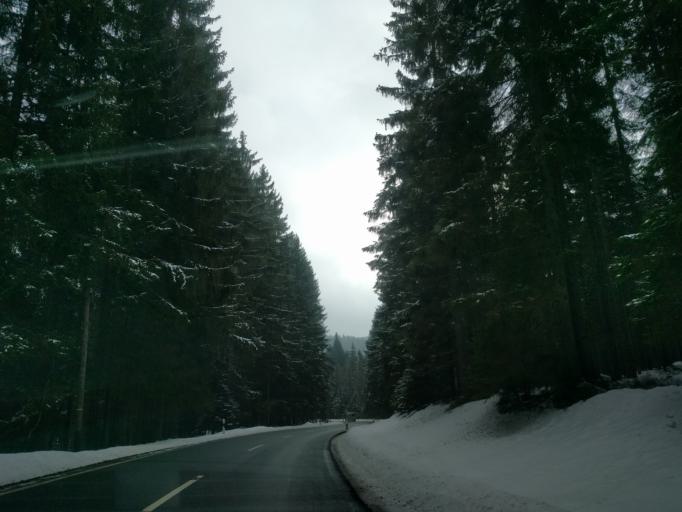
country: DE
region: Bavaria
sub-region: Lower Bavaria
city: Lindberg
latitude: 49.0487
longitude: 13.2567
